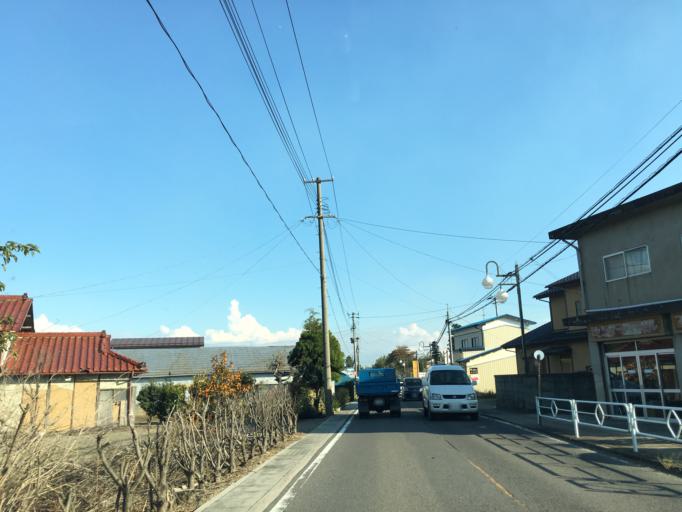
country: JP
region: Fukushima
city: Koriyama
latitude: 37.3954
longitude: 140.2744
